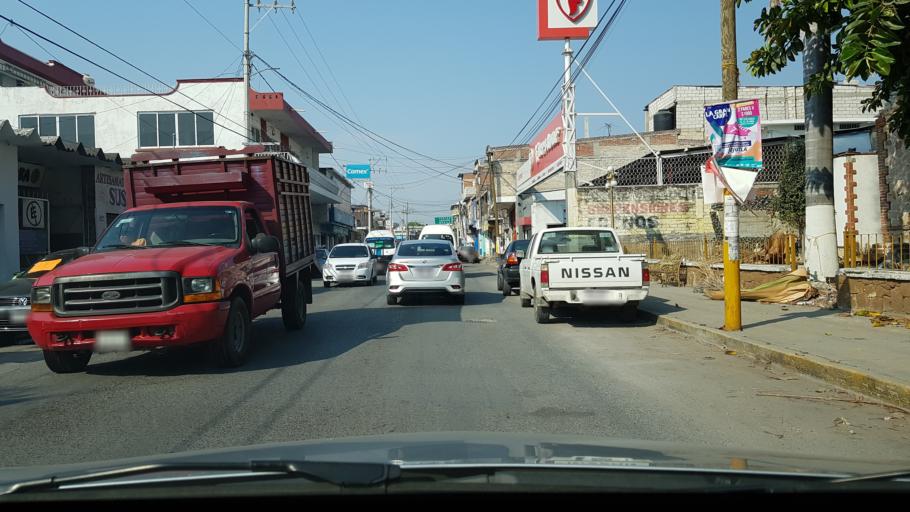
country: MX
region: Morelos
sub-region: Jojutla
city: Jojutla
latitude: 18.6182
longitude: -99.1749
